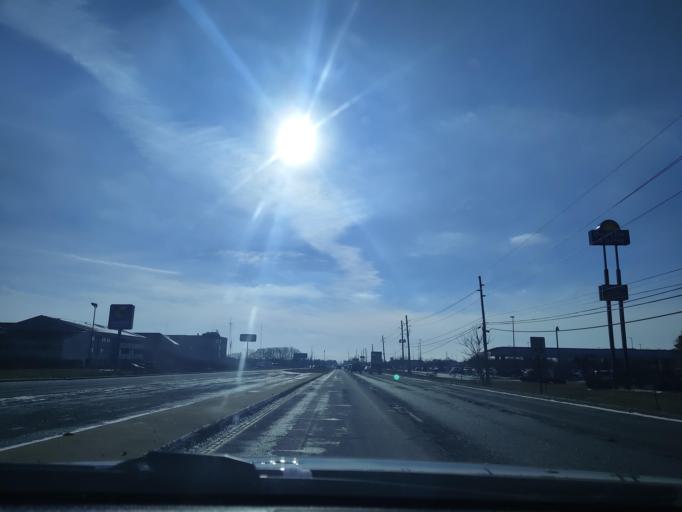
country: US
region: Indiana
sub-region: Boone County
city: Zionsville
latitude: 39.9193
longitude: -86.2264
